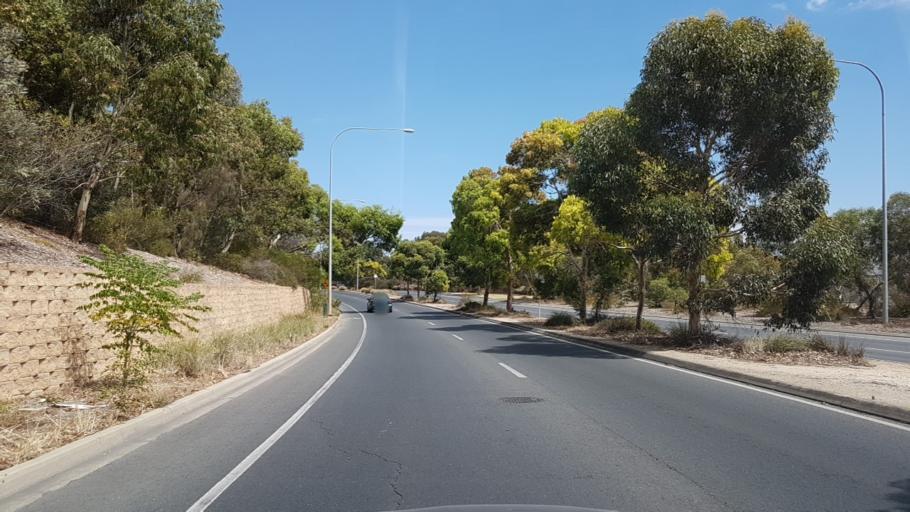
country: AU
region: South Australia
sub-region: City of West Torrens
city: Thebarton
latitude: -34.9286
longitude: 138.5774
